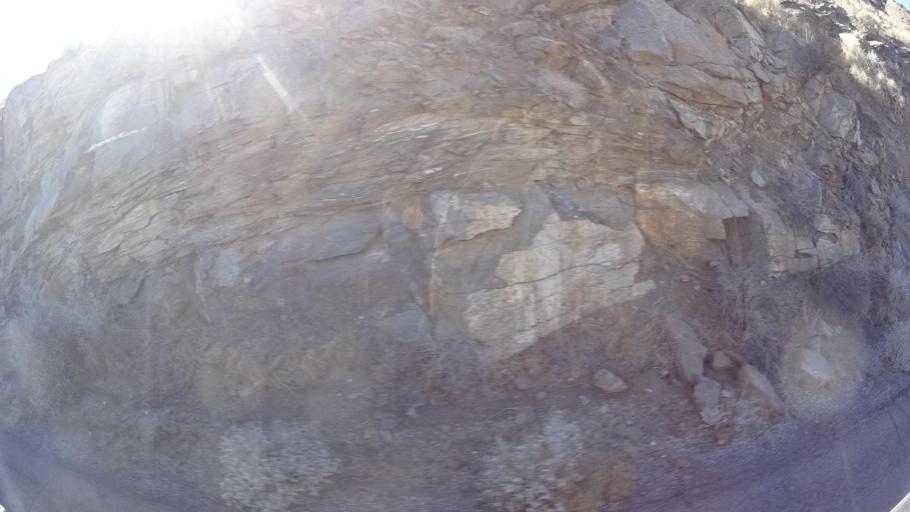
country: US
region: California
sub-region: Kern County
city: Ridgecrest
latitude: 35.3778
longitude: -117.6683
